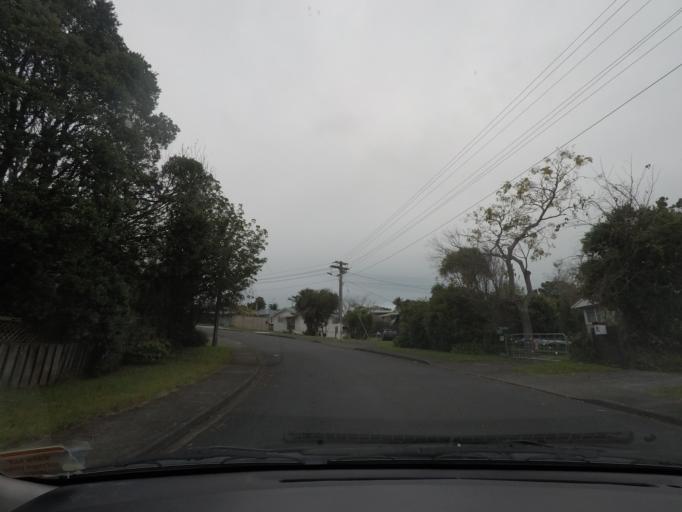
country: NZ
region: Auckland
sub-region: Auckland
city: Rosebank
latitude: -36.8607
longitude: 174.6398
